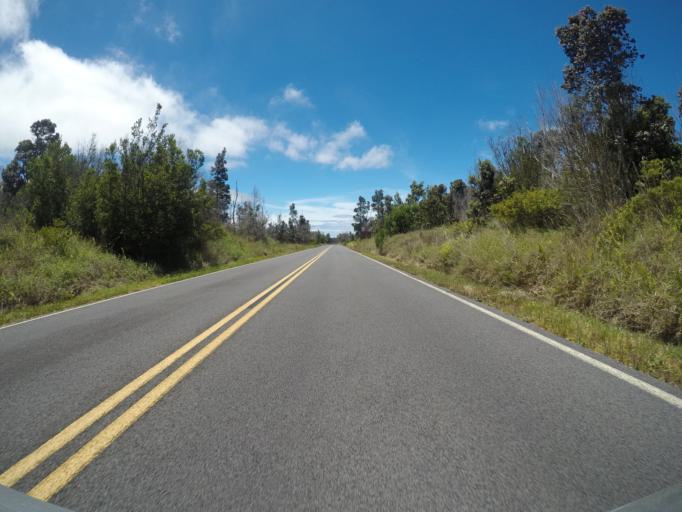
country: US
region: Hawaii
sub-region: Hawaii County
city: Volcano
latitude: 19.3786
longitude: -155.2389
